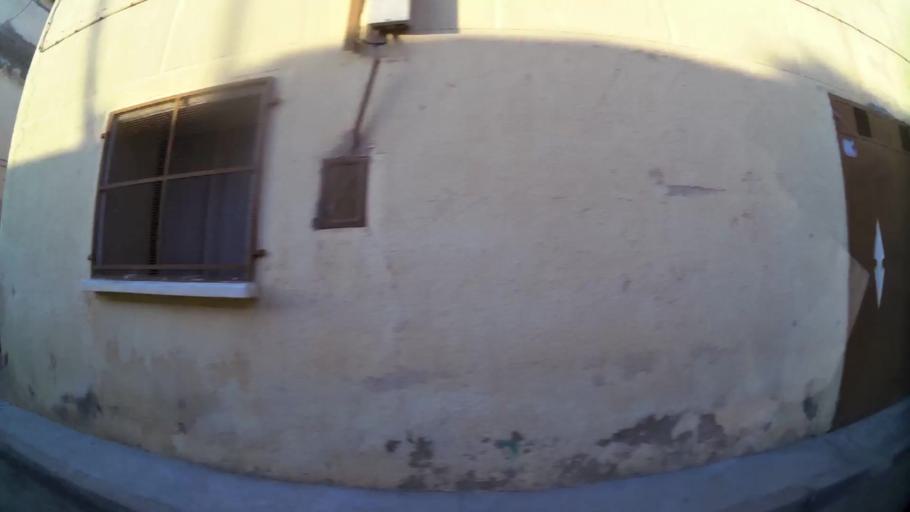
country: MA
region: Oriental
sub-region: Oujda-Angad
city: Oujda
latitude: 34.7034
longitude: -1.9240
